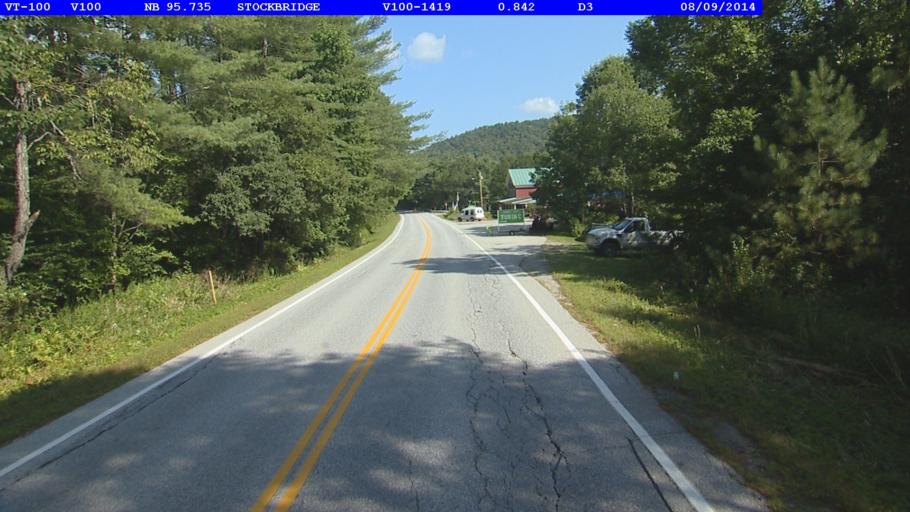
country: US
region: Vermont
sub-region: Orange County
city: Randolph
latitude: 43.7783
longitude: -72.7824
